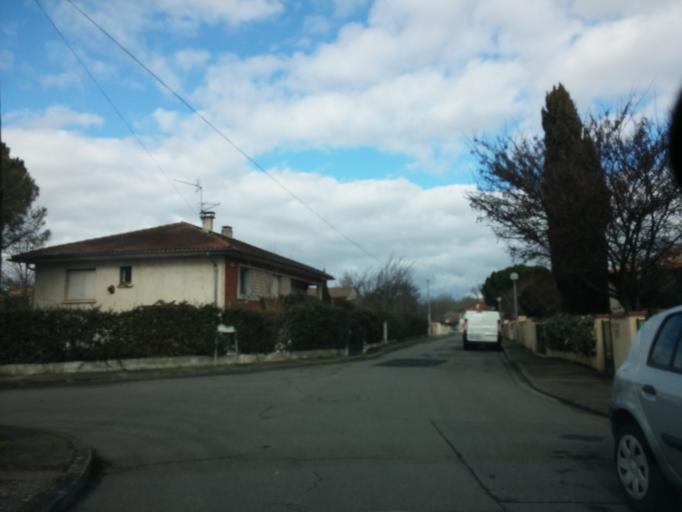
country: FR
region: Midi-Pyrenees
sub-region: Departement de la Haute-Garonne
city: Blagnac
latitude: 43.6403
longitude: 1.3982
